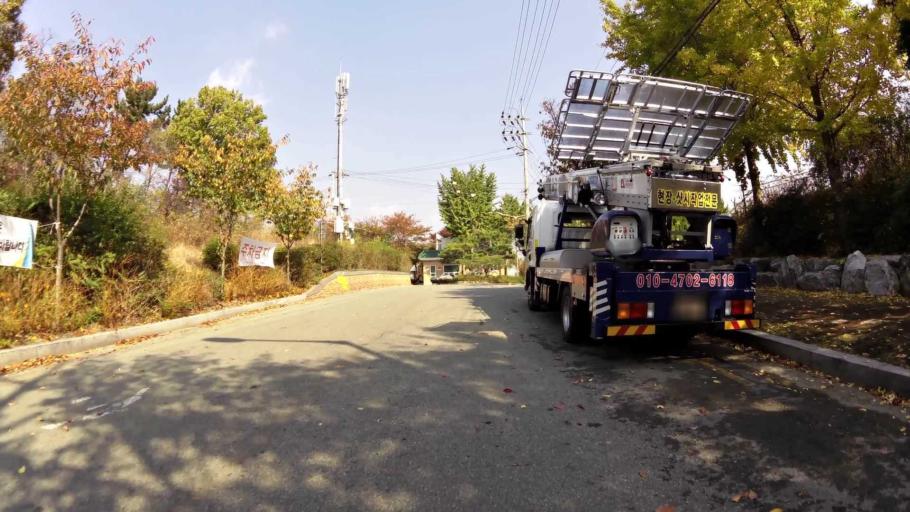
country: KR
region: Daegu
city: Daegu
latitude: 35.8564
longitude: 128.6588
